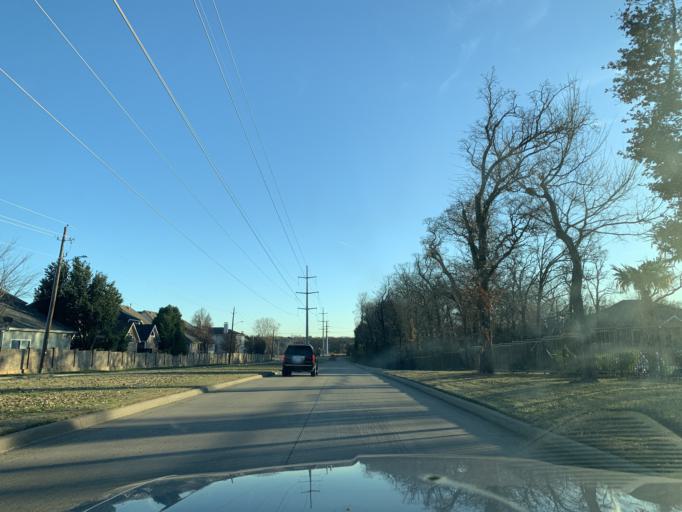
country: US
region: Texas
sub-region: Tarrant County
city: Euless
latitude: 32.8706
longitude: -97.0959
